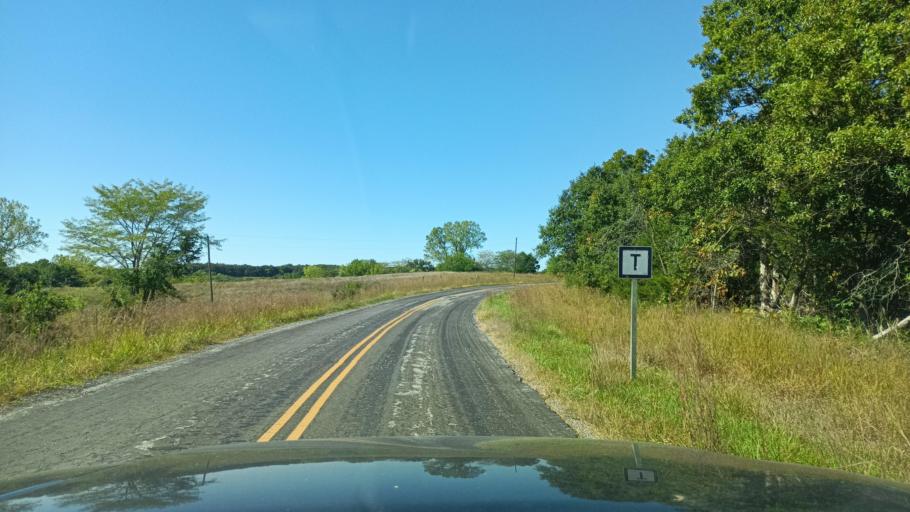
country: US
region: Missouri
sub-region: Scotland County
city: Memphis
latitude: 40.3534
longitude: -92.3505
